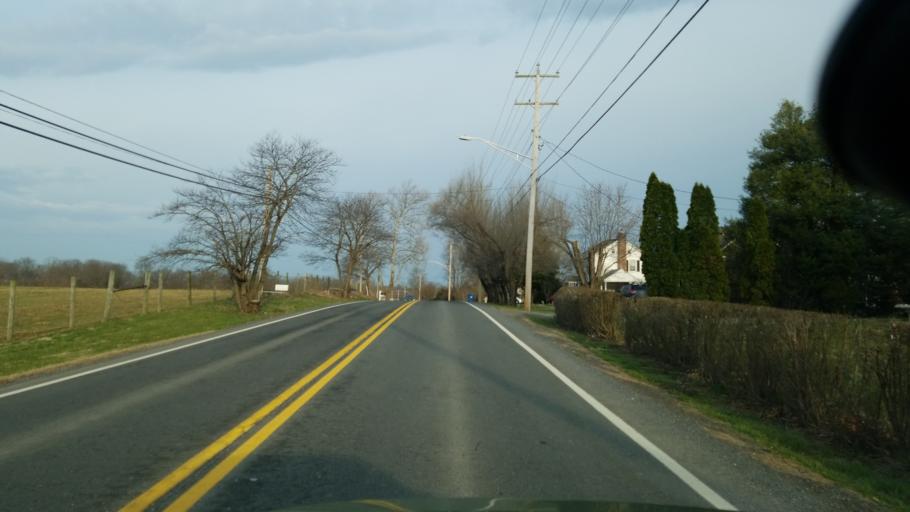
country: US
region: Virginia
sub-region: Clarke County
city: Berryville
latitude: 39.1455
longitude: -77.9638
